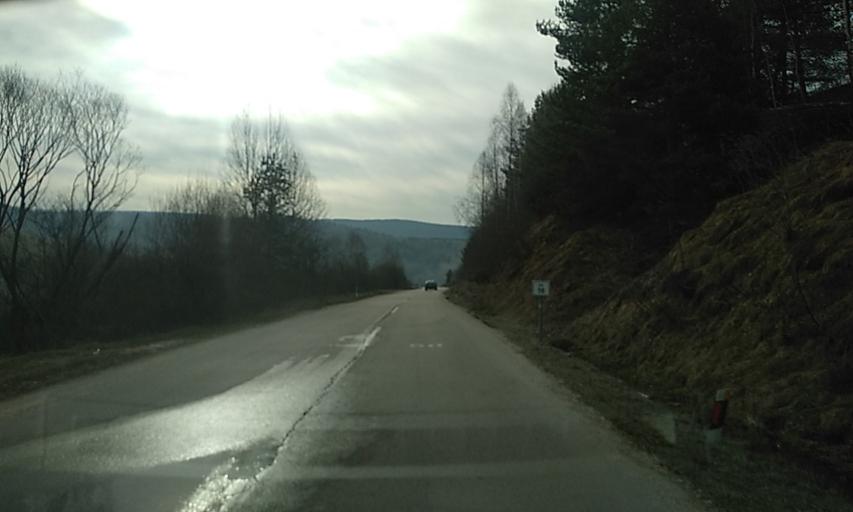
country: RS
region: Central Serbia
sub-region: Pcinjski Okrug
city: Bosilegrad
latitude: 42.6322
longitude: 22.3884
